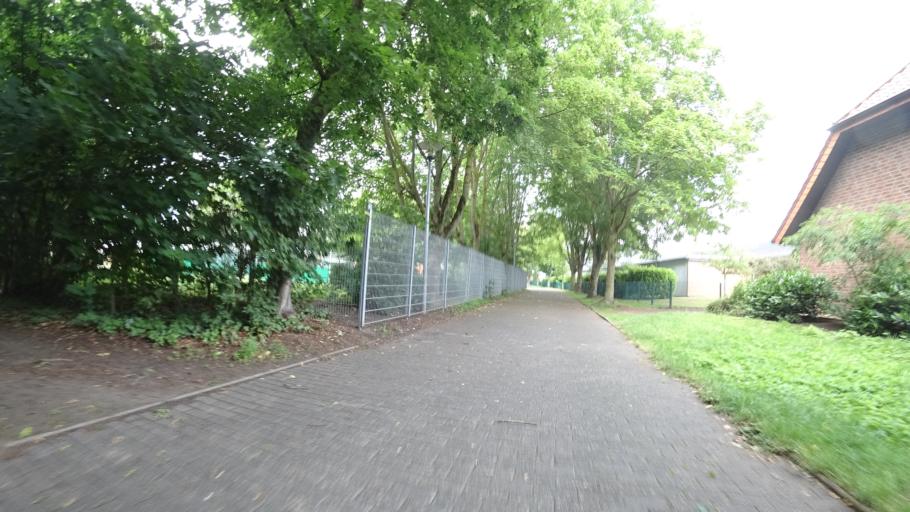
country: DE
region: North Rhine-Westphalia
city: Rietberg
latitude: 51.8142
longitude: 8.4257
